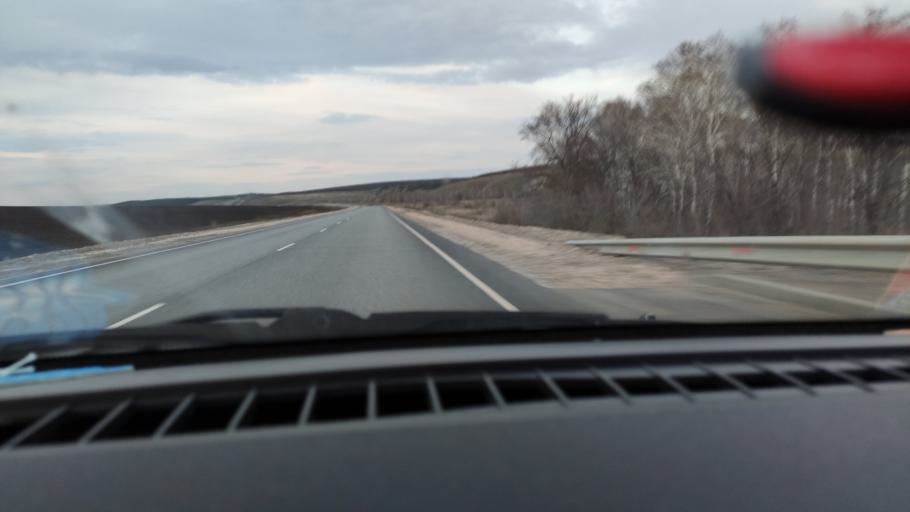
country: RU
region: Saratov
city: Yelshanka
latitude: 51.8589
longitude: 46.4974
